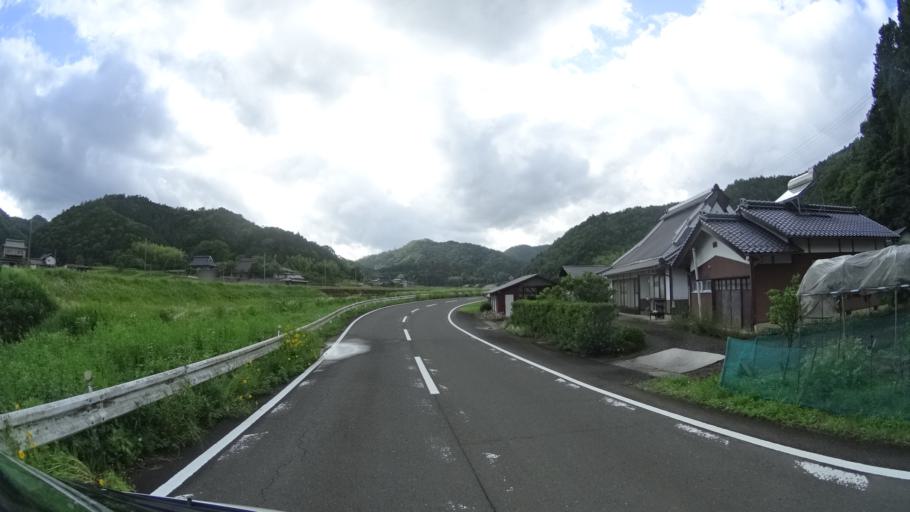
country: JP
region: Kyoto
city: Ayabe
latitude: 35.3764
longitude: 135.2229
